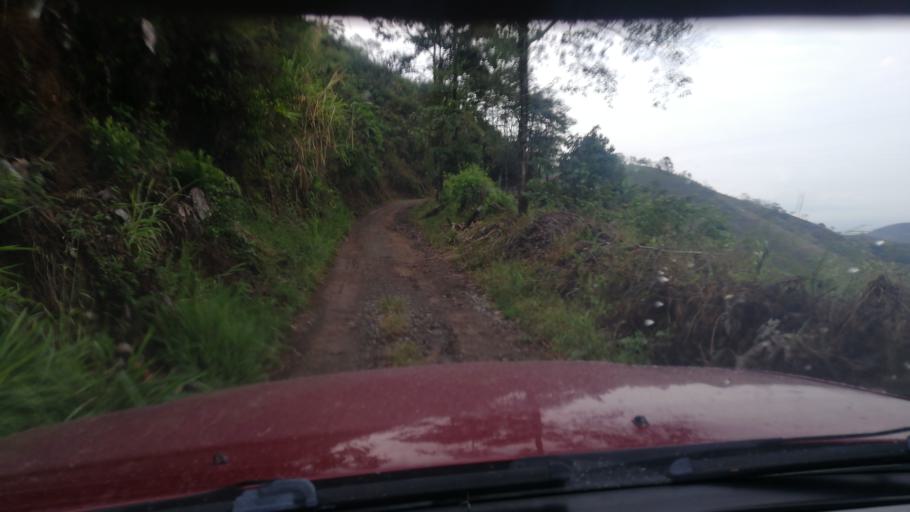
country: CO
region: Risaralda
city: Balboa
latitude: 4.8887
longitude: -75.9556
